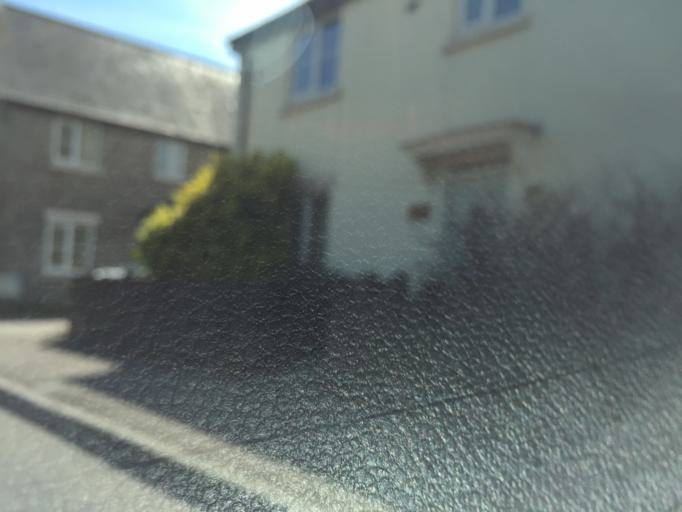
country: GB
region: England
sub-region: South Gloucestershire
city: Severn Beach
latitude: 51.5417
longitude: -2.6228
